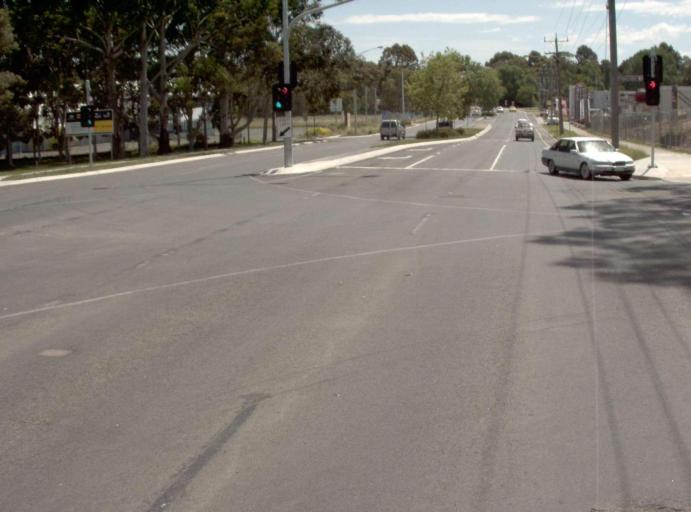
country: AU
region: Victoria
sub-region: Wellington
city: Sale
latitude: -38.1116
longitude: 147.0615
